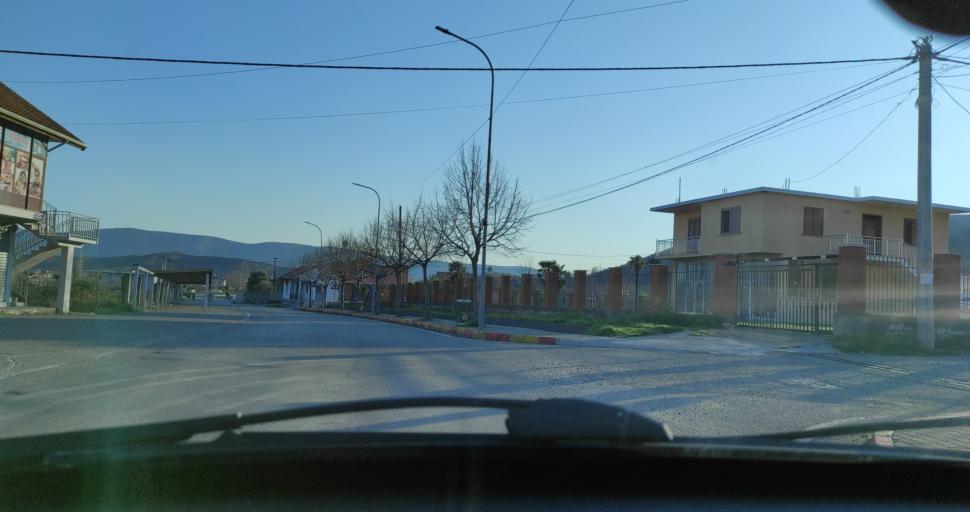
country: AL
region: Shkoder
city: Vukatane
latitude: 41.9583
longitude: 19.5330
